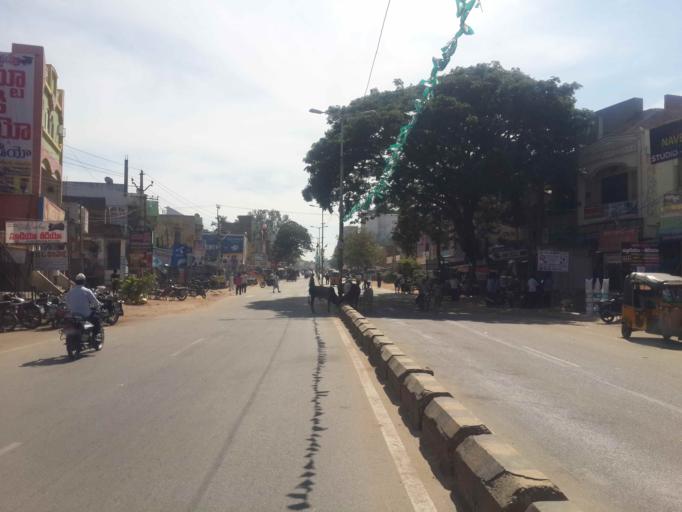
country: IN
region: Andhra Pradesh
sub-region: Anantapur
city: Kadiri
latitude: 14.1172
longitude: 78.1567
